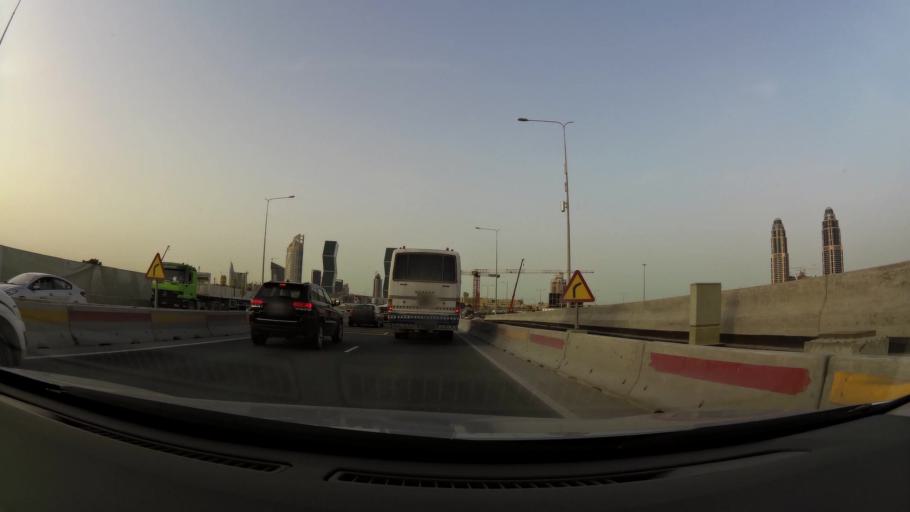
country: QA
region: Baladiyat ad Dawhah
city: Doha
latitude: 25.3685
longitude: 51.5238
